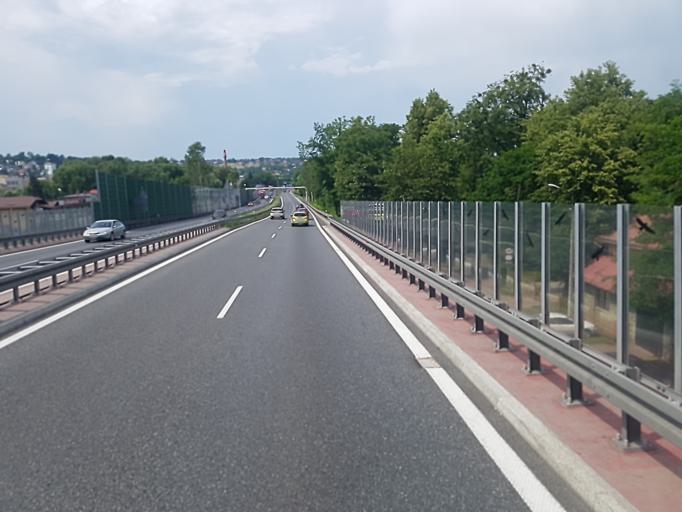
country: PL
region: Silesian Voivodeship
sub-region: Powiat cieszynski
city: Skoczow
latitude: 49.7978
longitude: 18.7936
